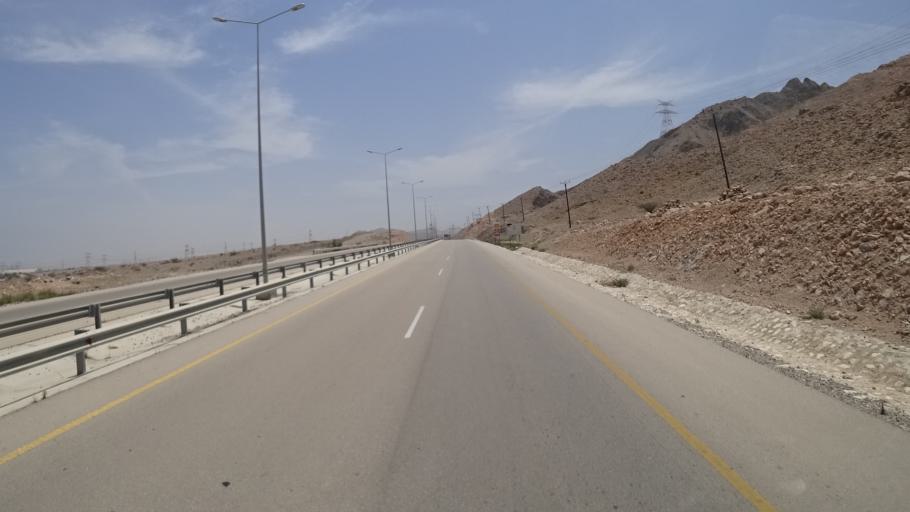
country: OM
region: Ash Sharqiyah
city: Sur
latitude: 22.6624
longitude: 59.3903
